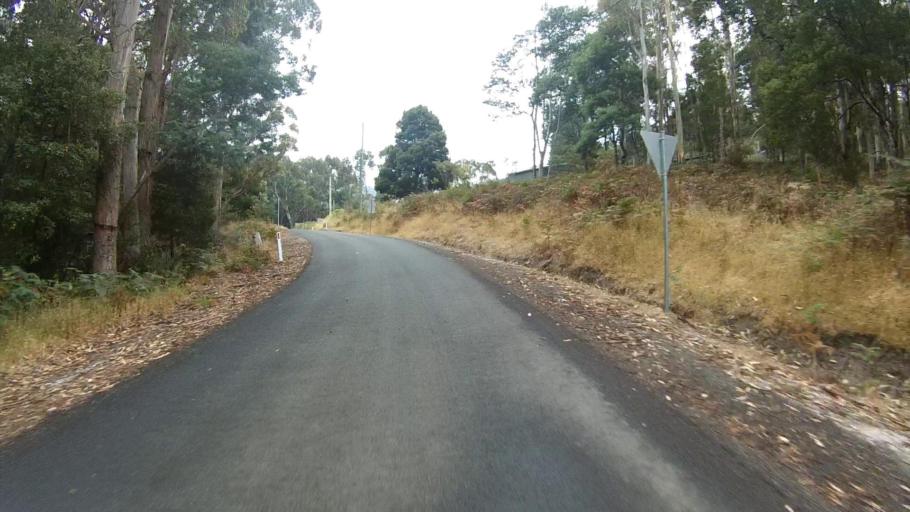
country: AU
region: Tasmania
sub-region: Huon Valley
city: Cygnet
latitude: -43.2364
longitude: 147.1562
